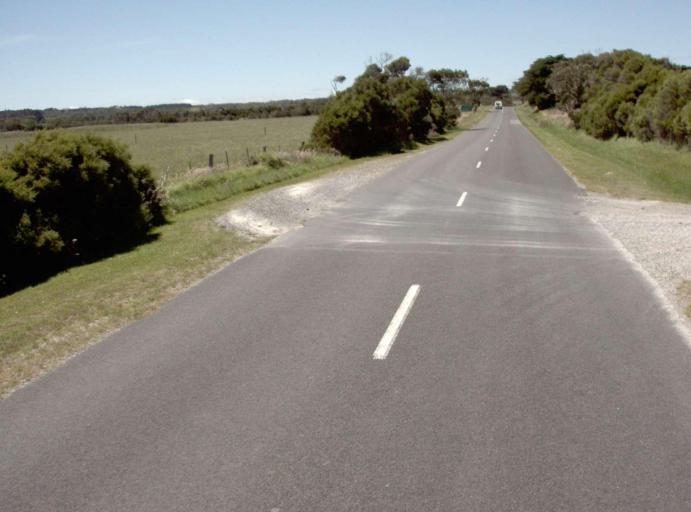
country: AU
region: Victoria
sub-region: Bass Coast
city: North Wonthaggi
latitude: -38.7992
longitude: 146.0861
